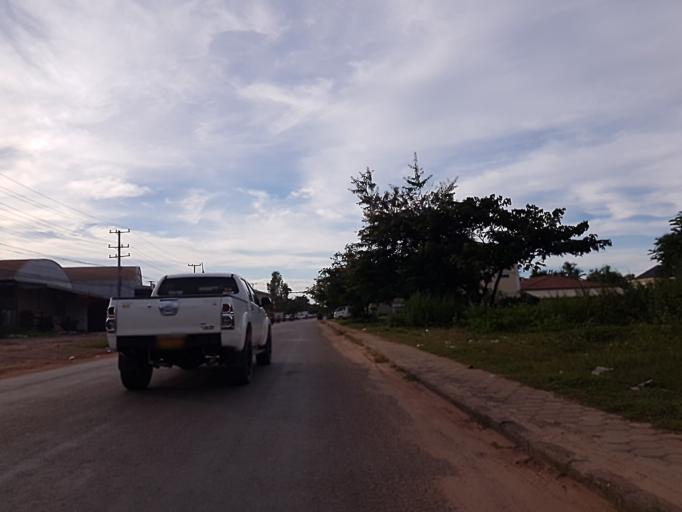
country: TH
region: Nong Khai
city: Si Chiang Mai
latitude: 18.0006
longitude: 102.5599
